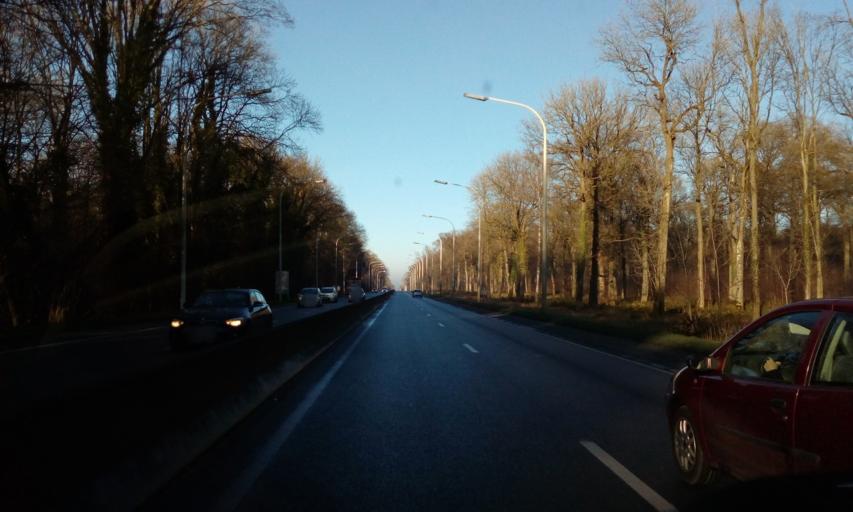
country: BE
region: Wallonia
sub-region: Province du Hainaut
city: Gerpinnes
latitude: 50.3478
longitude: 4.4724
